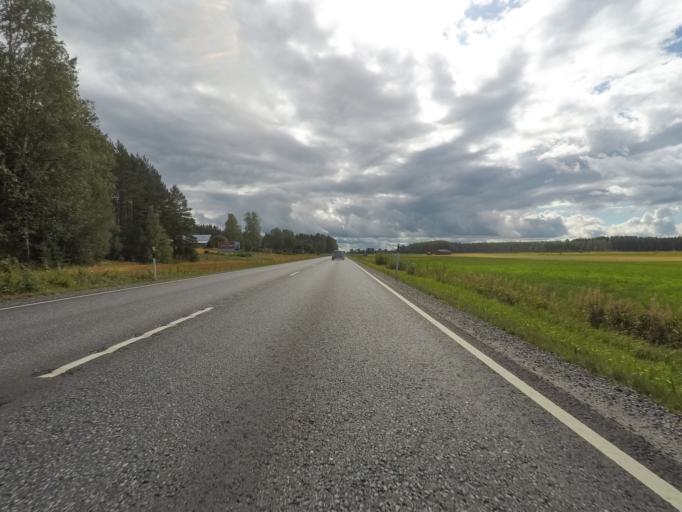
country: FI
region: Paijanne Tavastia
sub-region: Lahti
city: Hartola
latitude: 61.6256
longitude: 26.0114
